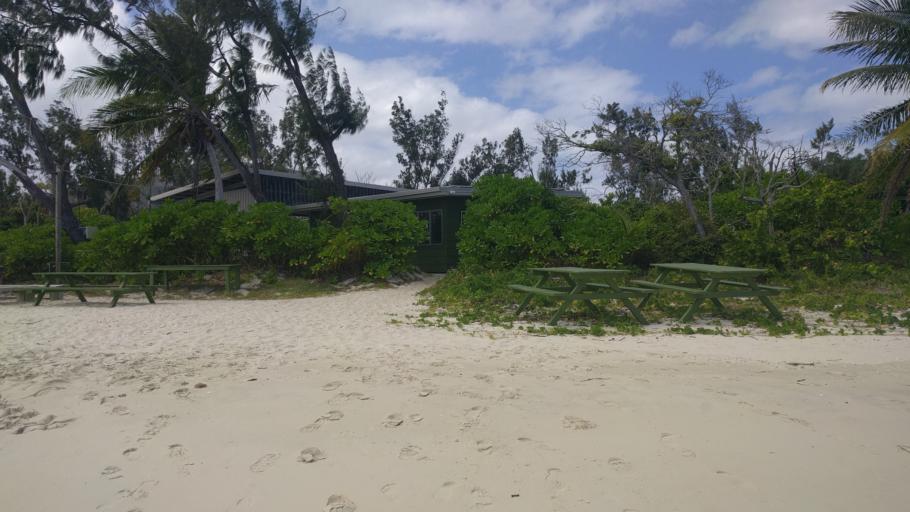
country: AU
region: Queensland
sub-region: Cook
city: Cooktown
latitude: -14.6795
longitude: 145.4475
